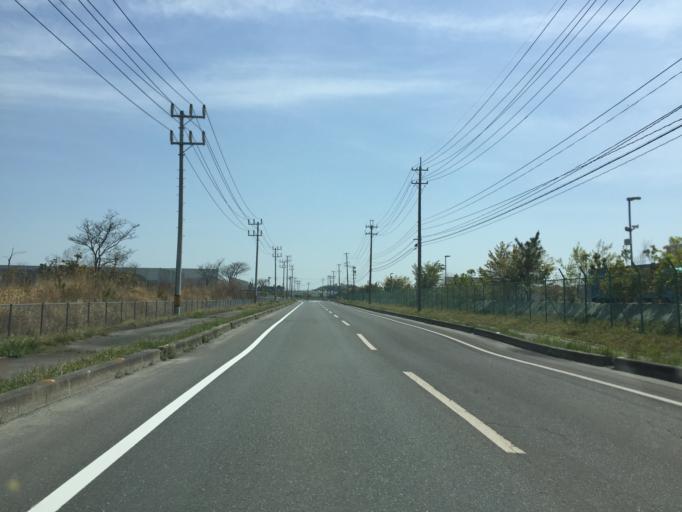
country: JP
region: Miyagi
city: Marumori
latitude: 37.8319
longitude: 140.9457
